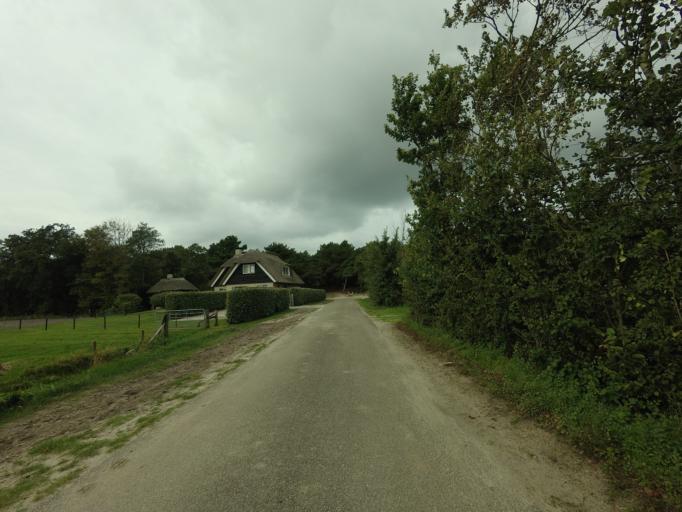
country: NL
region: Friesland
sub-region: Gemeente Ameland
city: Hollum
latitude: 53.4440
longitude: 5.6255
